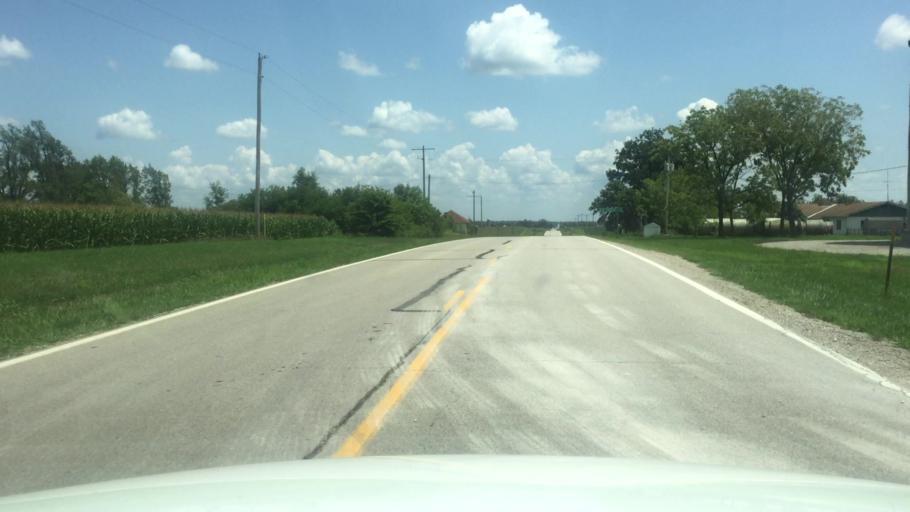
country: US
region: Kansas
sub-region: Brown County
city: Horton
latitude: 39.6674
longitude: -95.6040
